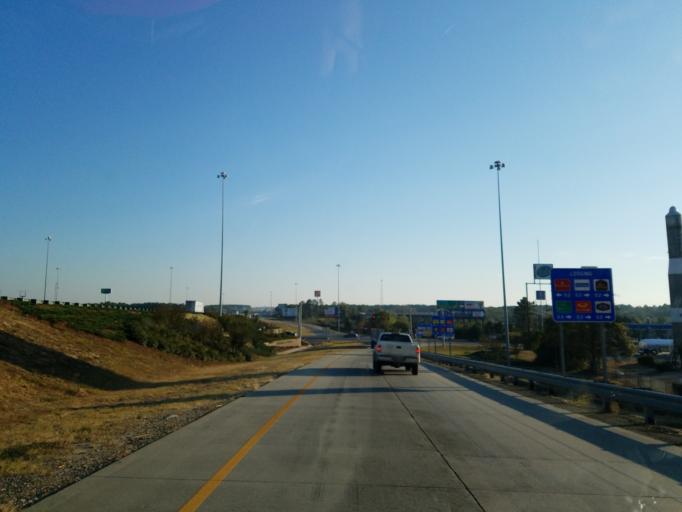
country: US
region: Georgia
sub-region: Crisp County
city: Cordele
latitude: 31.9616
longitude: -83.7521
